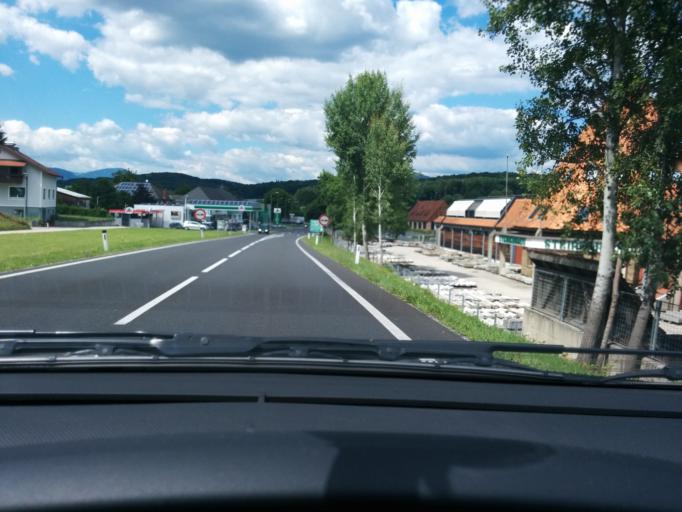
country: AT
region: Styria
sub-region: Politischer Bezirk Weiz
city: Oberrettenbach
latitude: 47.1484
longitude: 15.7701
